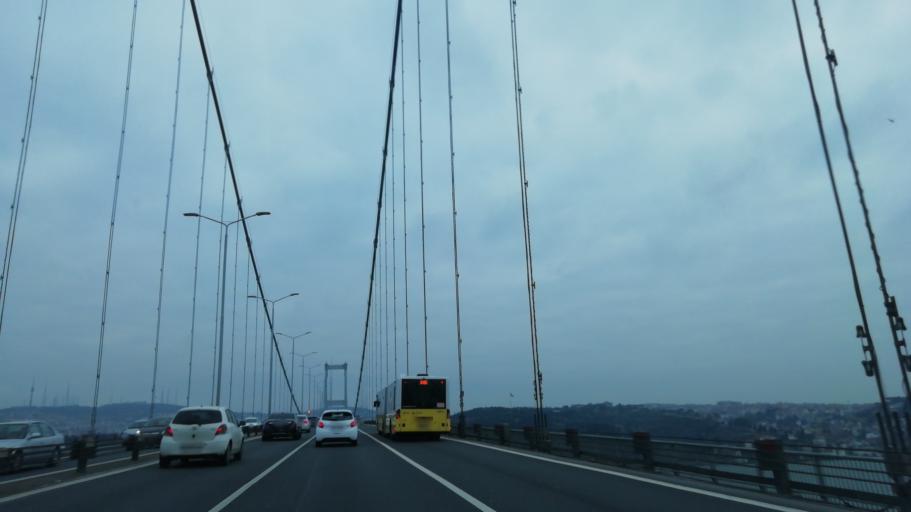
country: TR
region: Istanbul
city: UEskuedar
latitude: 41.0490
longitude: 29.0307
